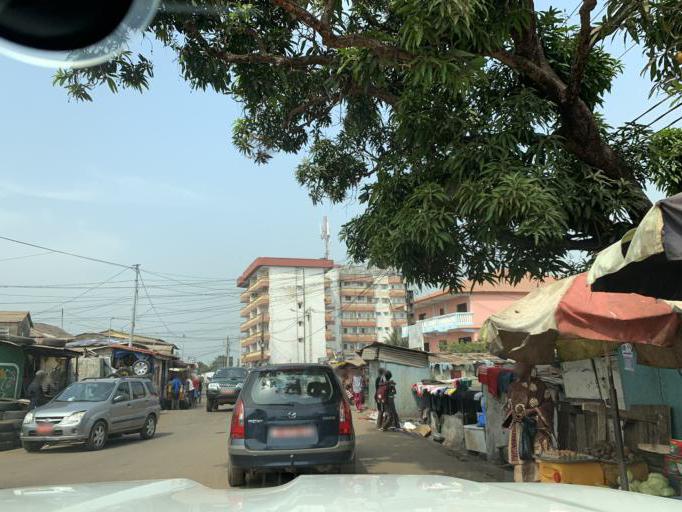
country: GN
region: Conakry
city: Conakry
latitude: 9.5543
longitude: -13.6688
